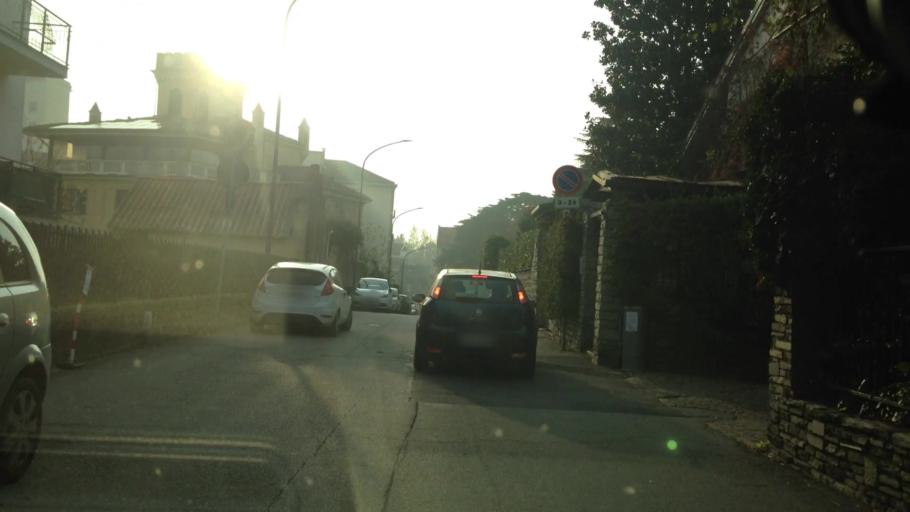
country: IT
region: Piedmont
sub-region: Provincia di Asti
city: Asti
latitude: 44.9067
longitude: 8.2050
